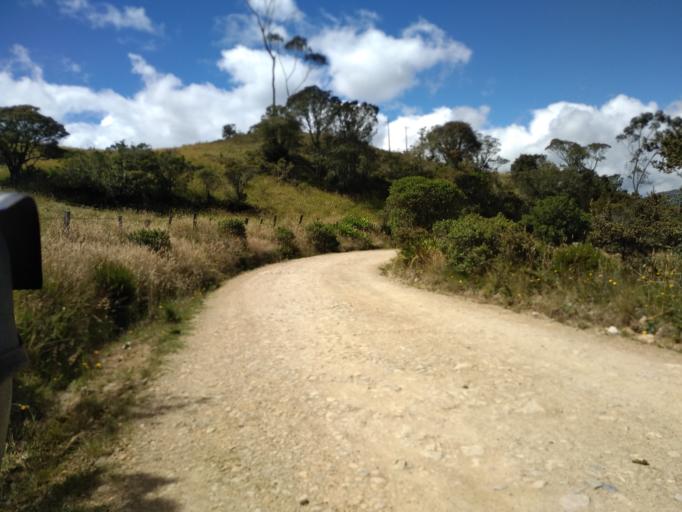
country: CO
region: Boyaca
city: Duitama
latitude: 5.9369
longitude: -73.1041
